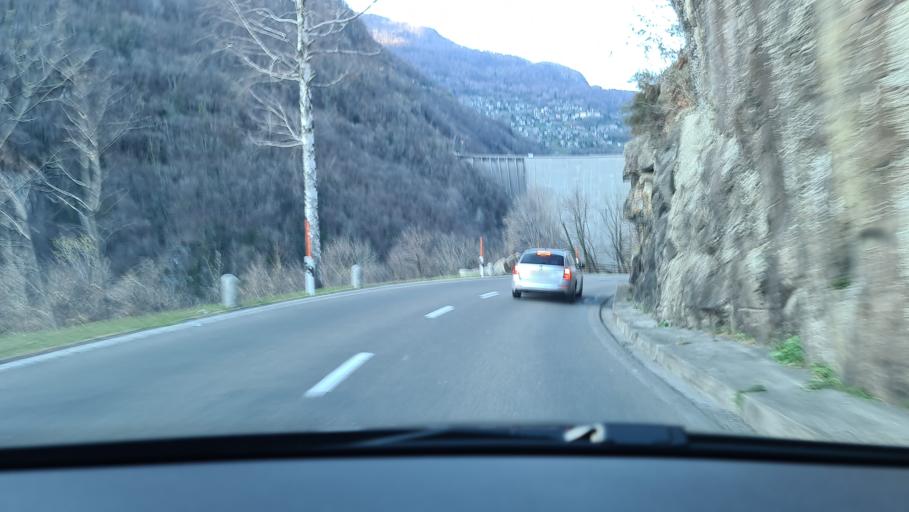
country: CH
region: Ticino
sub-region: Locarno District
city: Gordola
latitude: 46.1908
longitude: 8.8478
